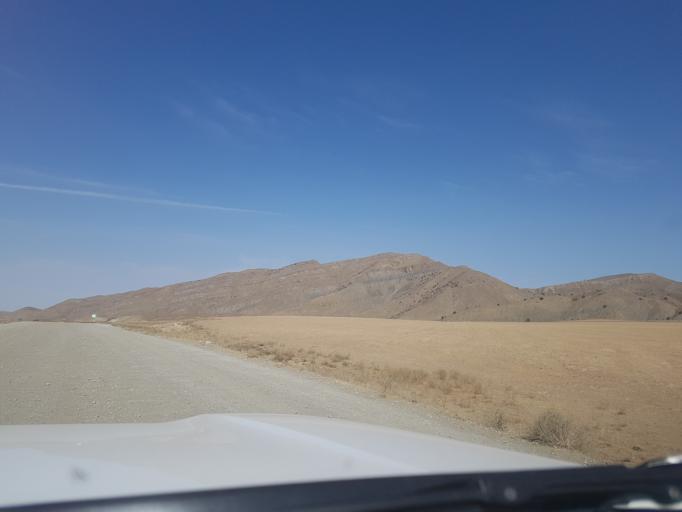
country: TM
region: Ahal
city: Baharly
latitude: 38.4366
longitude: 57.0405
